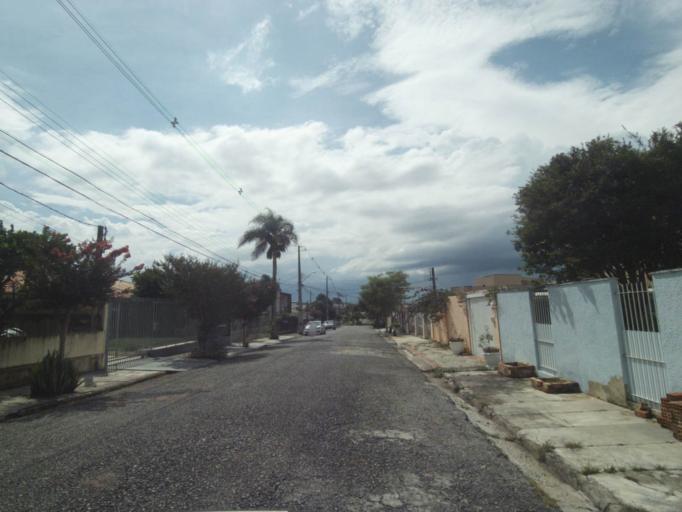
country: BR
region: Parana
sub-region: Pinhais
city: Pinhais
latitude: -25.4728
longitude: -49.2066
